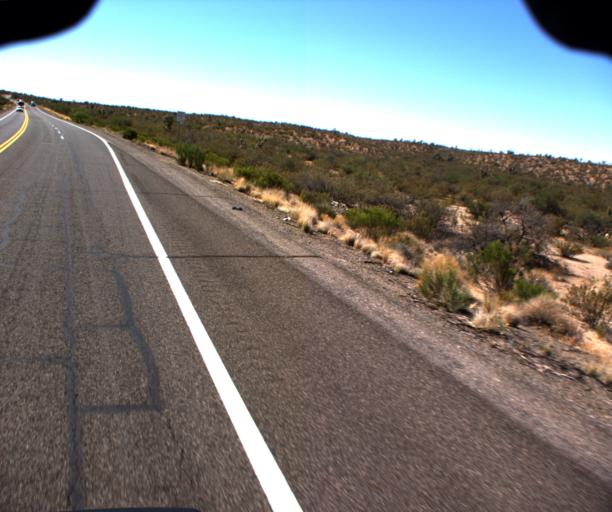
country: US
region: Arizona
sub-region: Yavapai County
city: Congress
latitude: 34.2032
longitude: -113.0631
